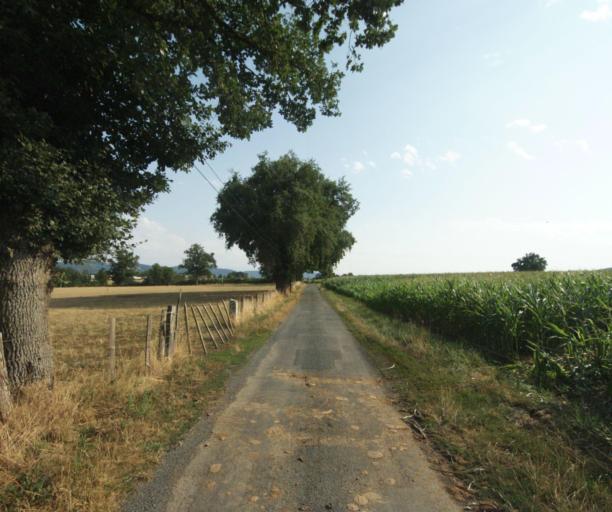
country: FR
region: Rhone-Alpes
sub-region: Departement du Rhone
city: Savigny
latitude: 45.8270
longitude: 4.5831
